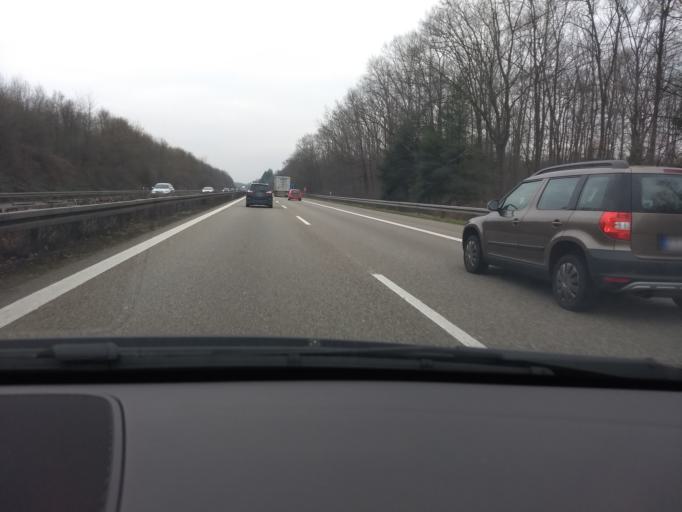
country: DE
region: Baden-Wuerttemberg
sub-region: Freiburg Region
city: Teningen
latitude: 48.1040
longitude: 7.7914
